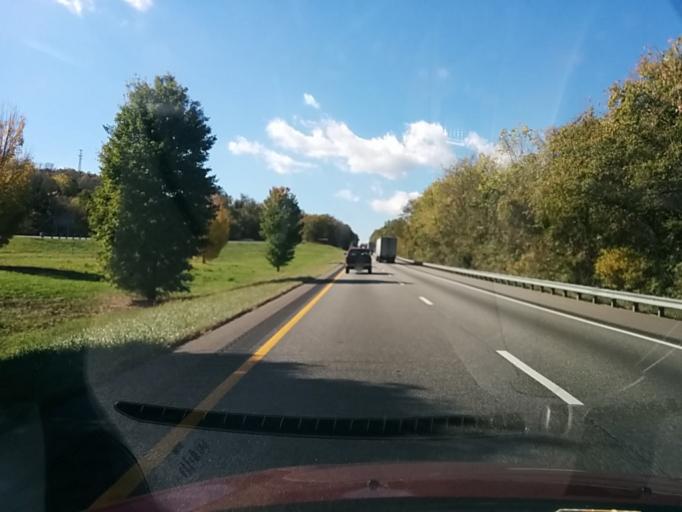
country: US
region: Virginia
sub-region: Botetourt County
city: Buchanan
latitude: 37.4884
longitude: -79.7711
